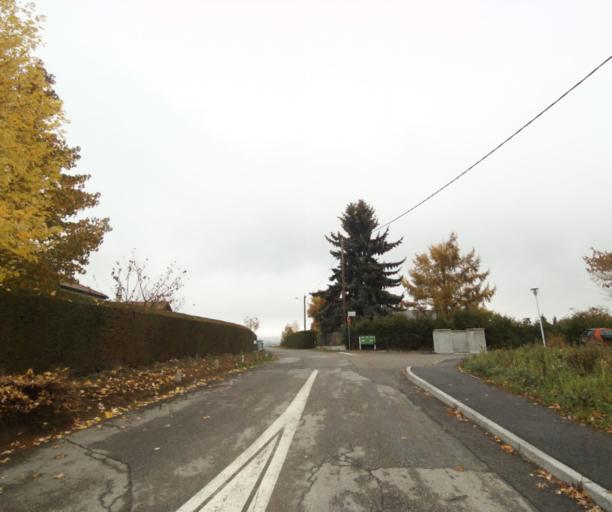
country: FR
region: Rhone-Alpes
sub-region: Departement de la Haute-Savoie
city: Reignier-Esery
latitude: 46.1358
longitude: 6.2913
